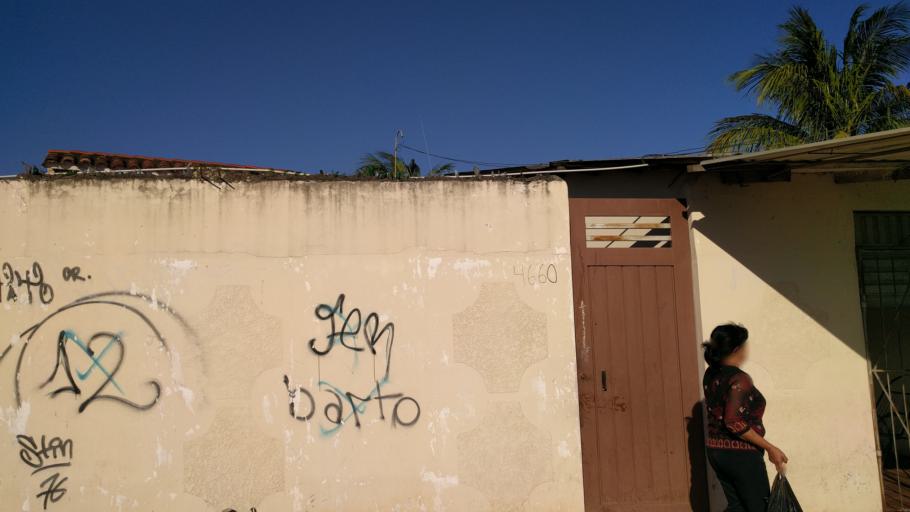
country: BO
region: Santa Cruz
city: Santa Cruz de la Sierra
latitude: -17.7410
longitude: -63.1896
